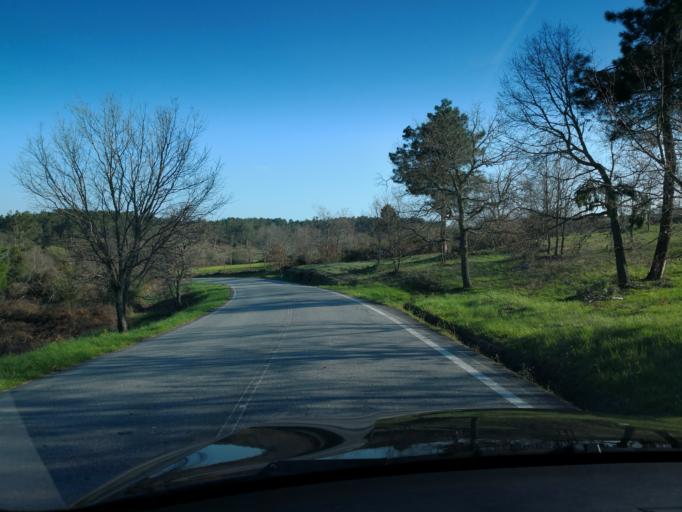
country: PT
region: Vila Real
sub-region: Sabrosa
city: Sabrosa
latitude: 41.3545
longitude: -7.6129
